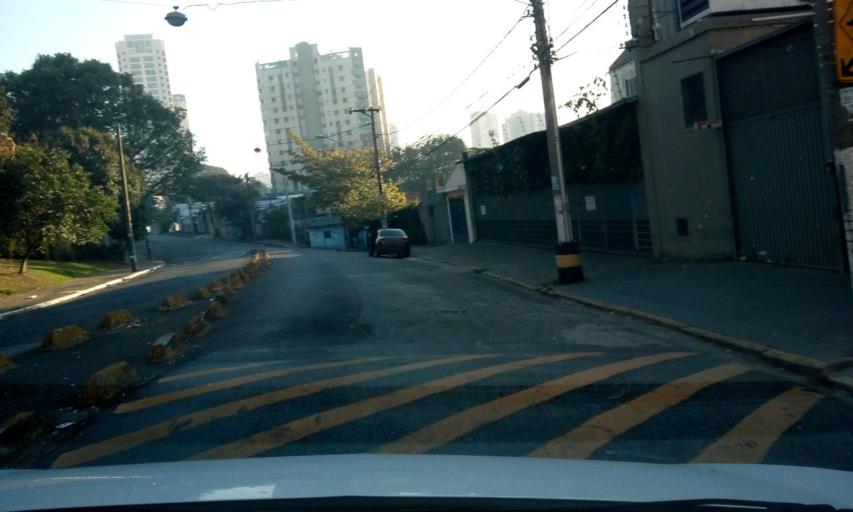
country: BR
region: Sao Paulo
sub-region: Sao Paulo
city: Sao Paulo
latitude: -23.5328
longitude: -46.6937
